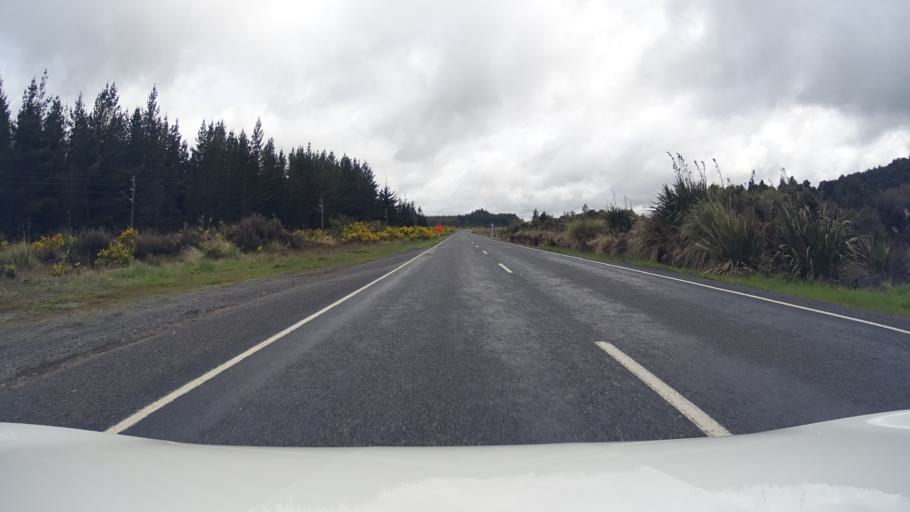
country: NZ
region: Manawatu-Wanganui
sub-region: Ruapehu District
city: Waiouru
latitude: -39.2198
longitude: 175.4008
